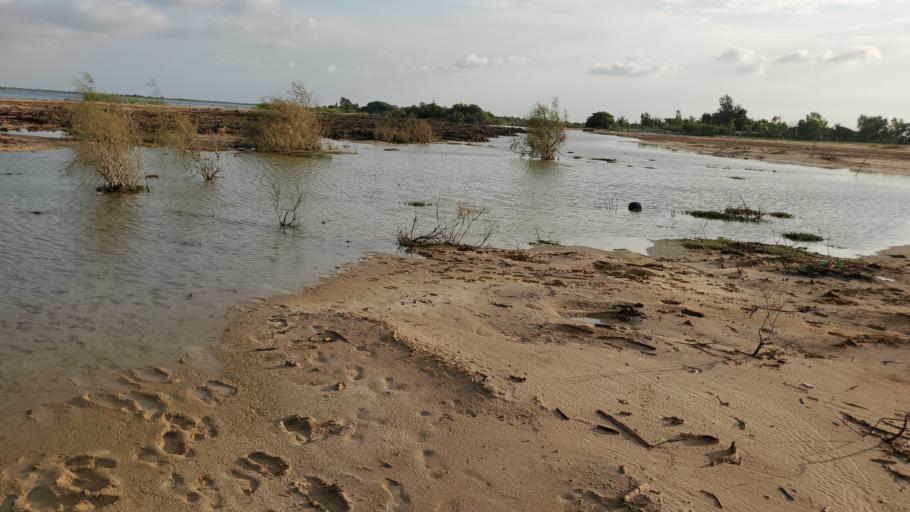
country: SN
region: Saint-Louis
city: Saint-Louis
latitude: 16.0462
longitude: -16.4155
